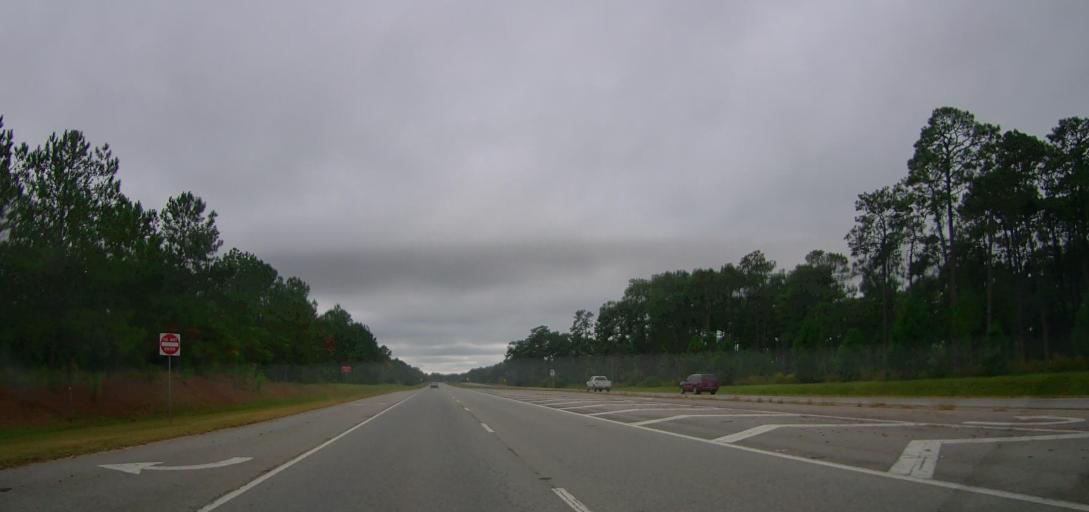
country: US
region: Georgia
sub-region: Thomas County
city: Thomasville
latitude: 30.8371
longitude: -84.0070
